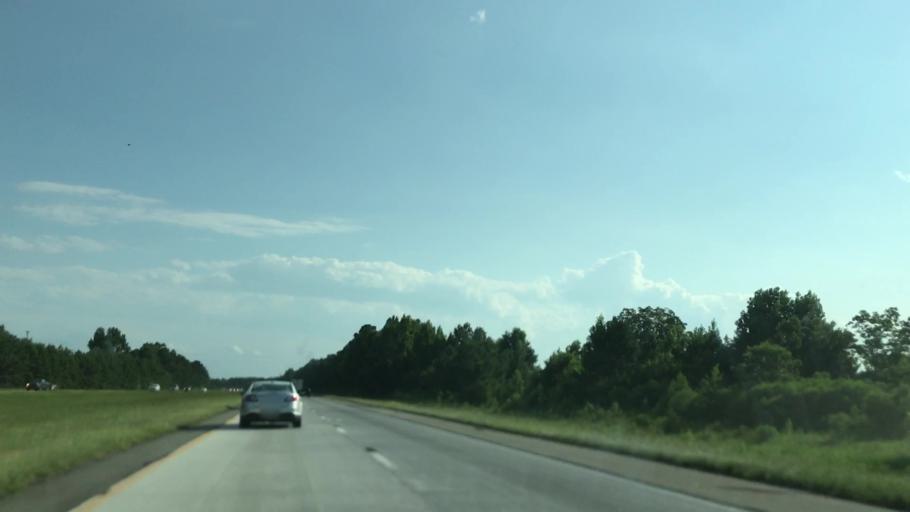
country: US
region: South Carolina
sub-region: Dorchester County
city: Saint George
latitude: 33.1382
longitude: -80.6327
